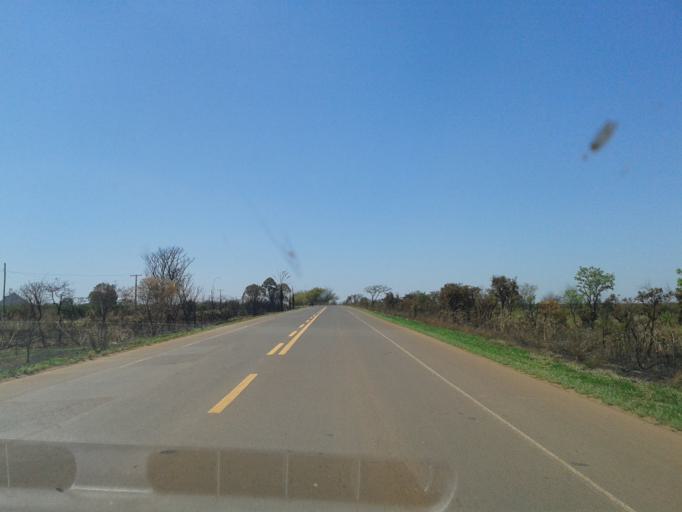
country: BR
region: Minas Gerais
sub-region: Araxa
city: Araxa
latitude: -19.4146
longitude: -47.3007
